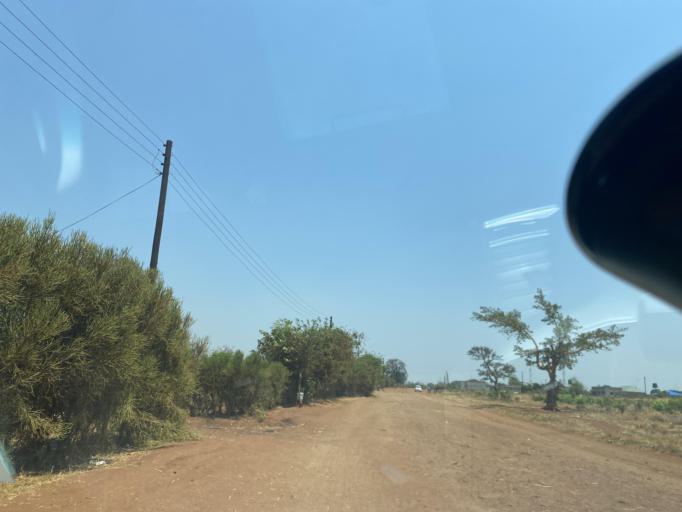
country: ZM
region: Southern
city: Nakambala
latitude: -15.5160
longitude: 27.9345
